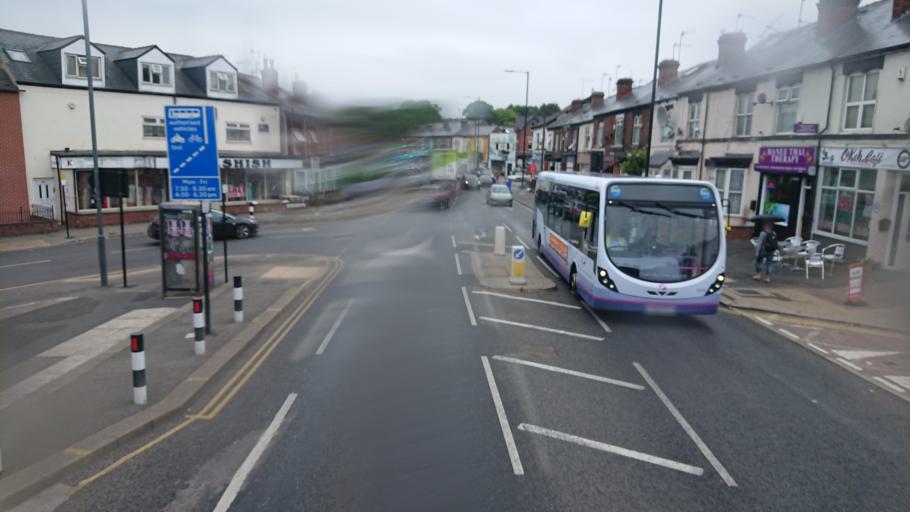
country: GB
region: England
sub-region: Sheffield
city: Sheffield
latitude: 53.3640
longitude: -1.4764
